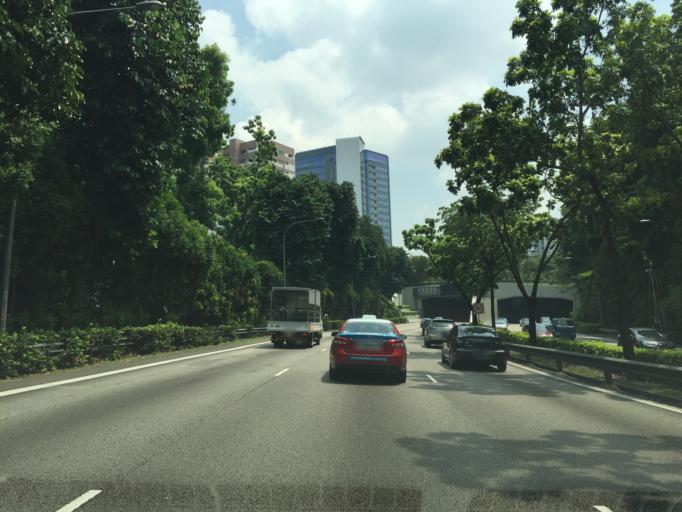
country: SG
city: Singapore
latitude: 1.3047
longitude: 103.8400
